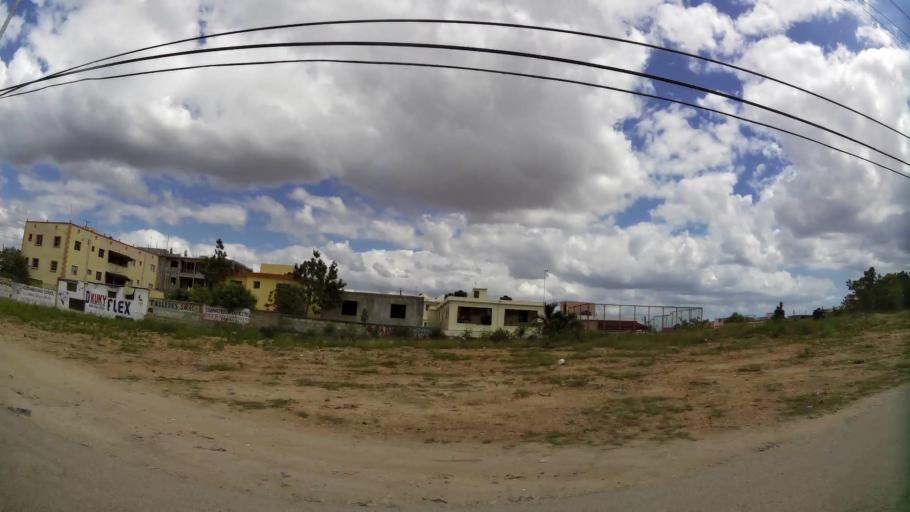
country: DO
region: Nacional
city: Ensanche Luperon
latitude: 18.5262
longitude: -69.8959
